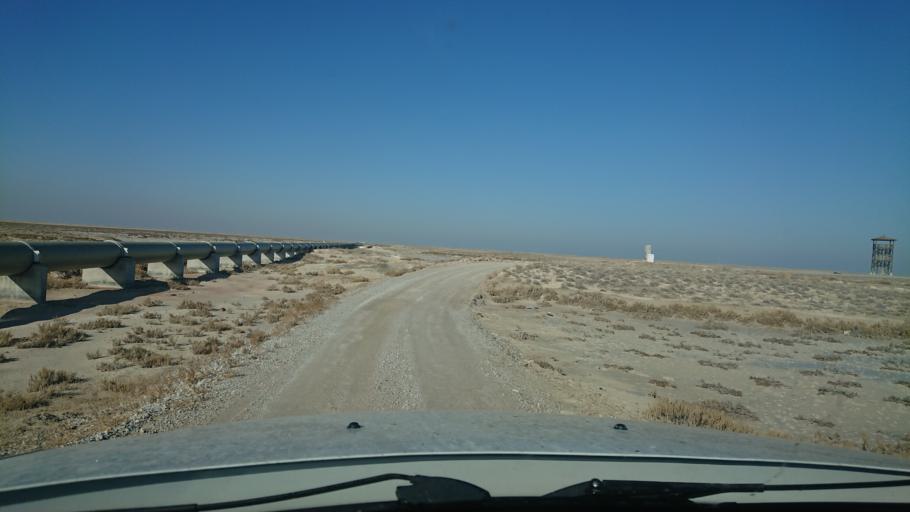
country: TR
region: Aksaray
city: Eskil
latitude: 38.4233
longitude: 33.5006
